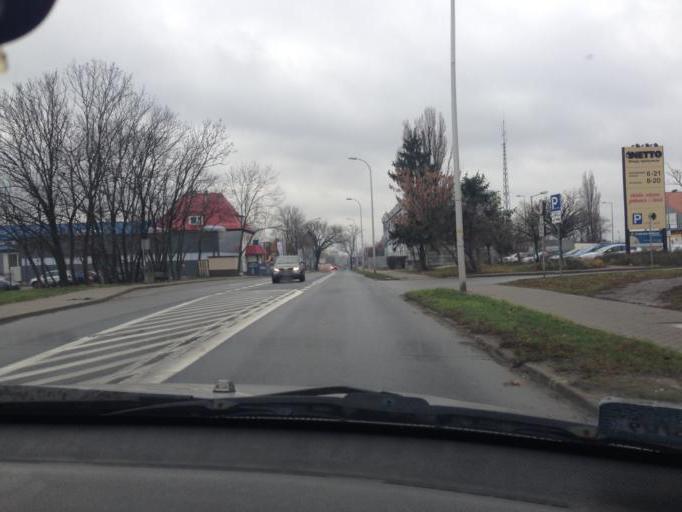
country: PL
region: Opole Voivodeship
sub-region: Powiat opolski
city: Opole
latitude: 50.6809
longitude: 17.9395
